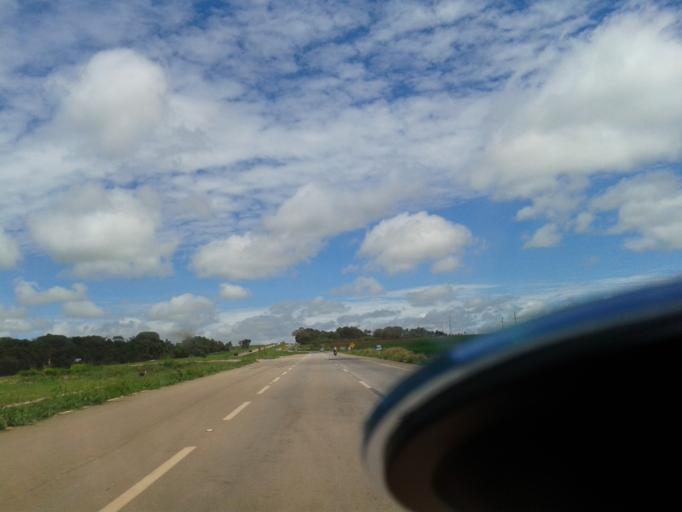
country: BR
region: Goias
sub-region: Inhumas
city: Inhumas
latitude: -16.2637
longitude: -49.5478
